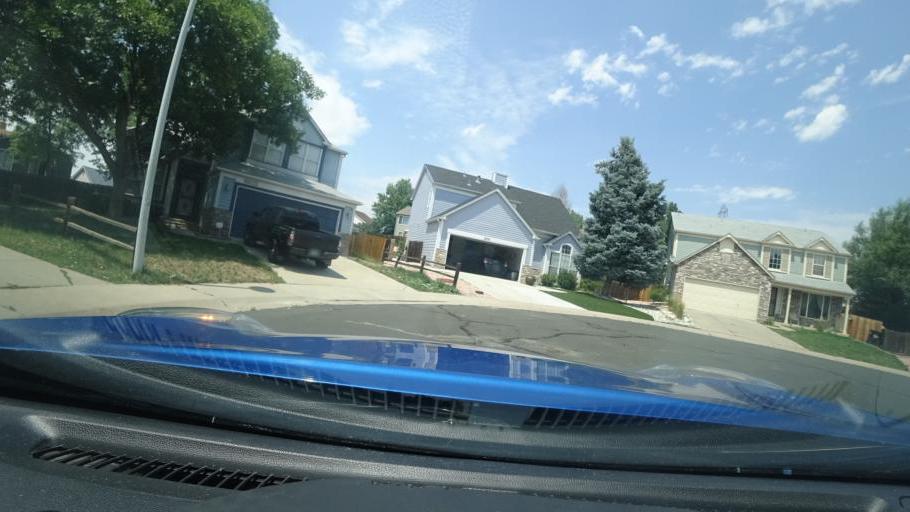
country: US
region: Colorado
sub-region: Adams County
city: Aurora
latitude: 39.6664
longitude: -104.7631
